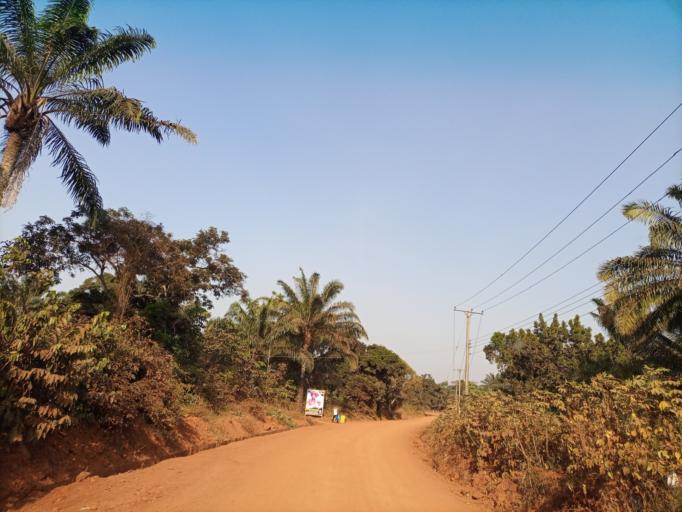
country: NG
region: Enugu
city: Opi
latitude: 6.7777
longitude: 7.3873
